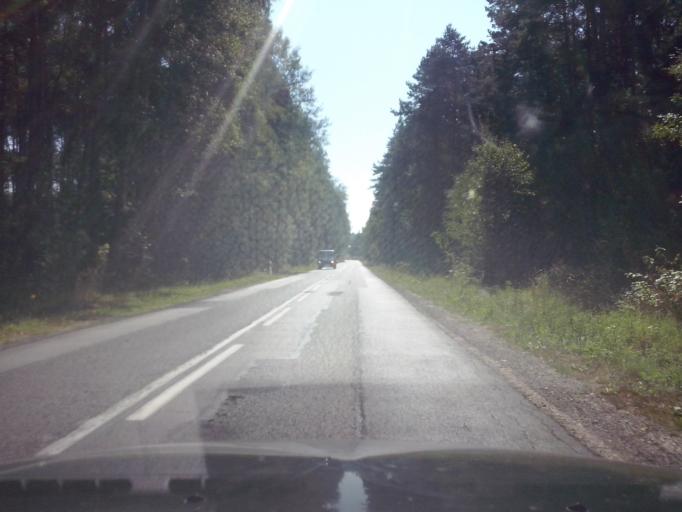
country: PL
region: Swietokrzyskie
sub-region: Powiat kielecki
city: Daleszyce
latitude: 50.8102
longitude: 20.7558
